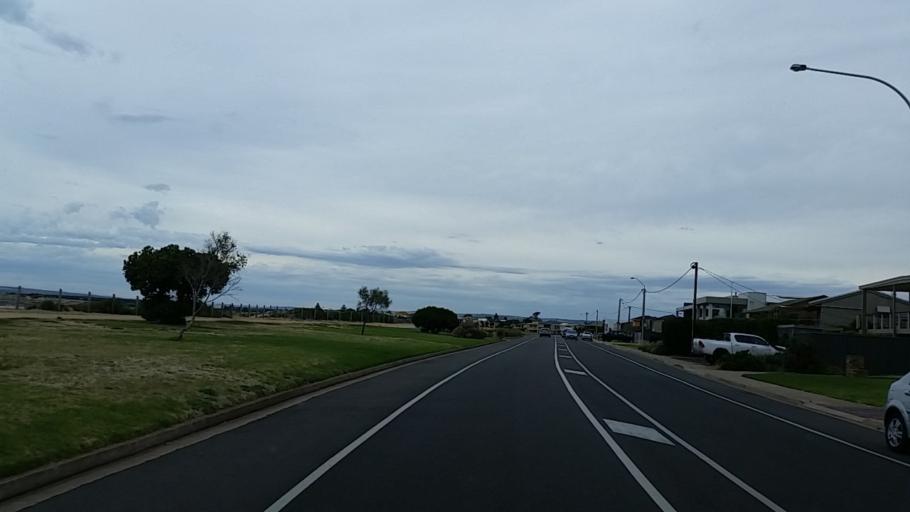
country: AU
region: South Australia
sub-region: Onkaparinga
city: Port Willunga
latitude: -35.2703
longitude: 138.4468
